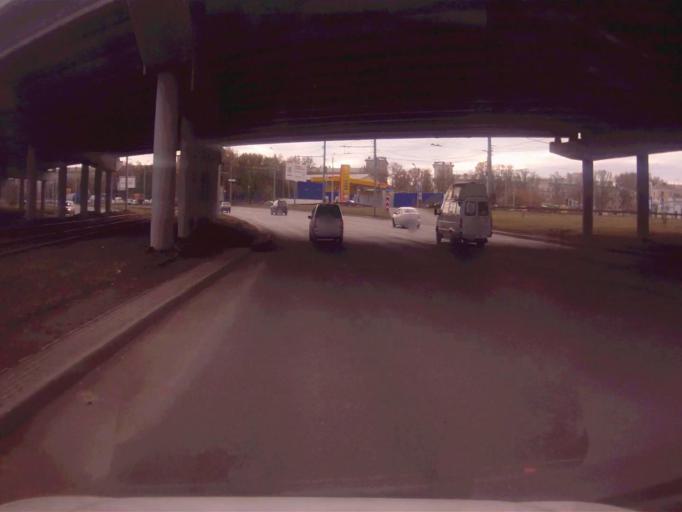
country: RU
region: Chelyabinsk
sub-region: Gorod Chelyabinsk
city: Chelyabinsk
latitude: 55.1510
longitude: 61.4422
